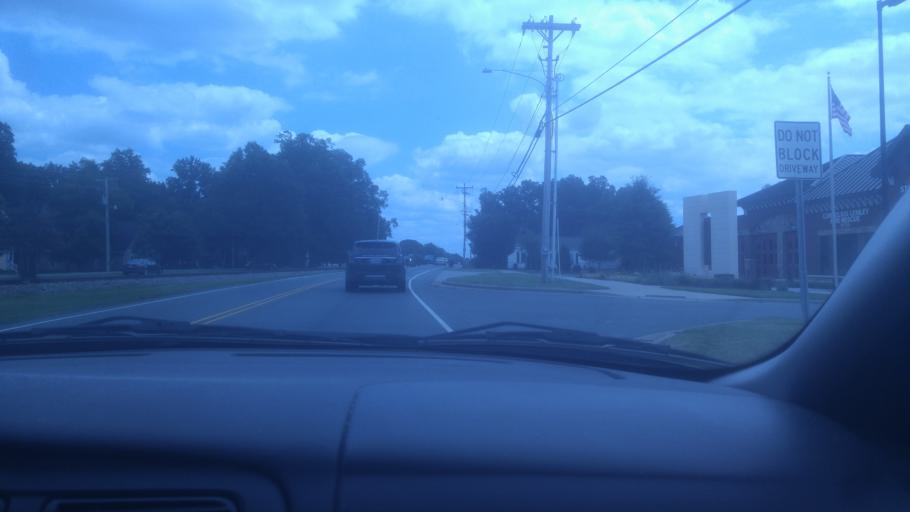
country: US
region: North Carolina
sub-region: Mecklenburg County
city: Cornelius
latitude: 35.4786
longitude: -80.8562
